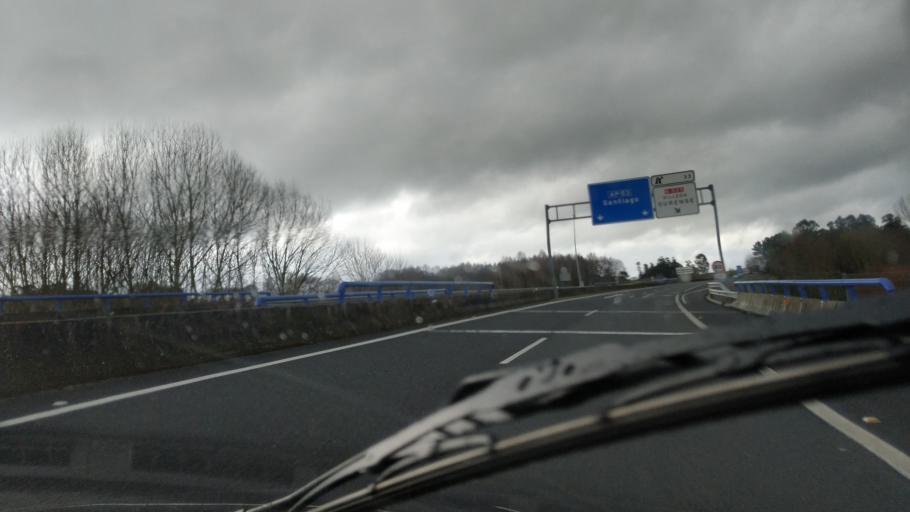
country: ES
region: Galicia
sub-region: Provincia de Pontevedra
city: Silleda
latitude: 42.7121
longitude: -8.2352
